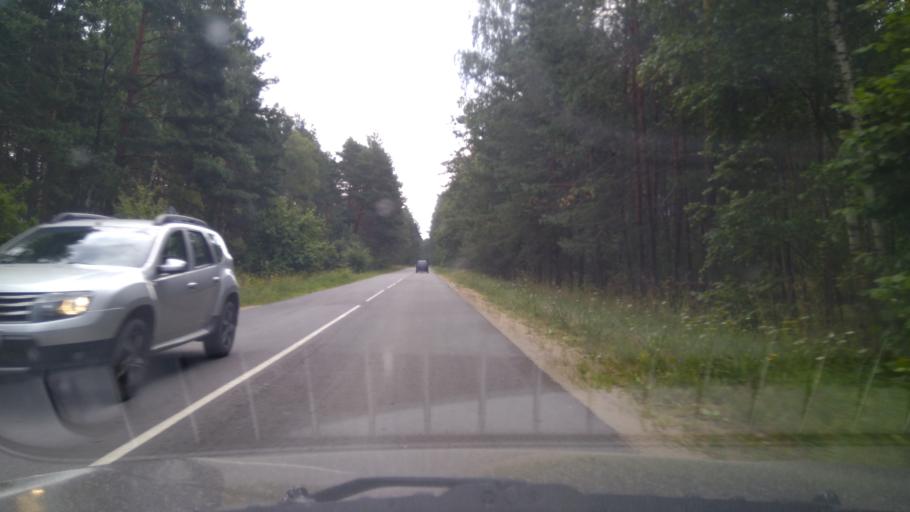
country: BY
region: Brest
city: Nyakhachava
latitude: 52.6017
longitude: 25.0925
